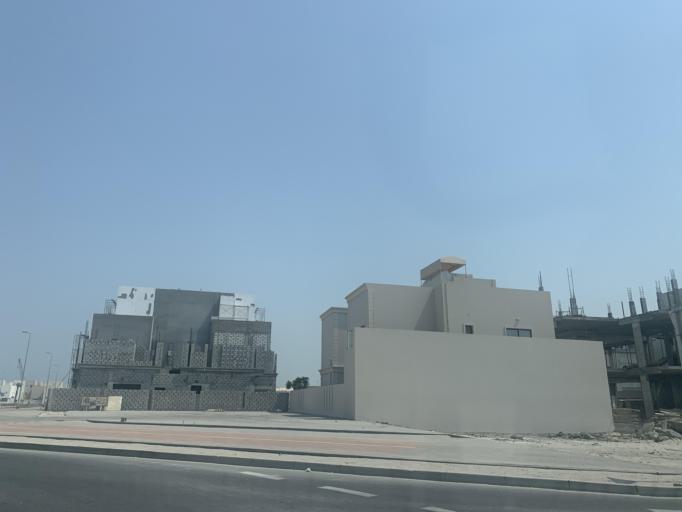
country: BH
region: Muharraq
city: Al Hadd
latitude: 26.2367
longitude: 50.6617
